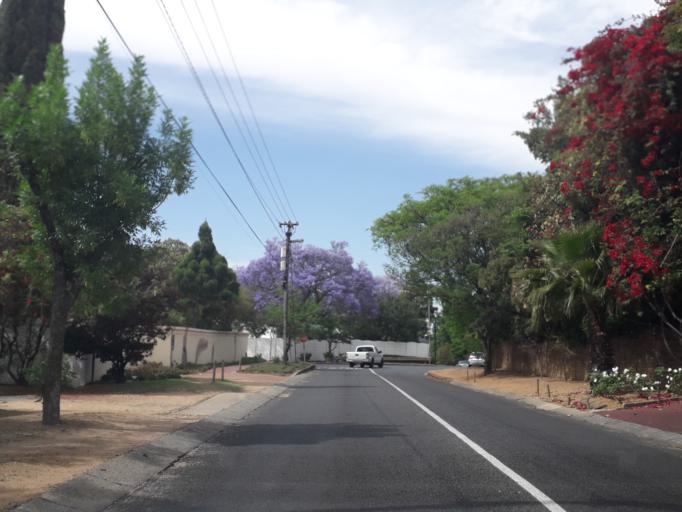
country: ZA
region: Gauteng
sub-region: City of Johannesburg Metropolitan Municipality
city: Johannesburg
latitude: -26.0726
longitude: 27.9986
